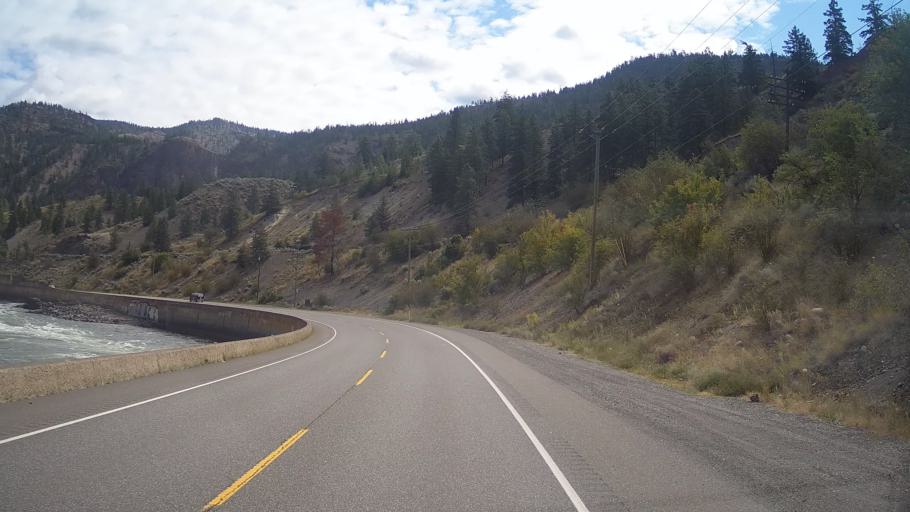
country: CA
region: British Columbia
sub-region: Thompson-Nicola Regional District
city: Ashcroft
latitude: 50.2632
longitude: -121.4081
